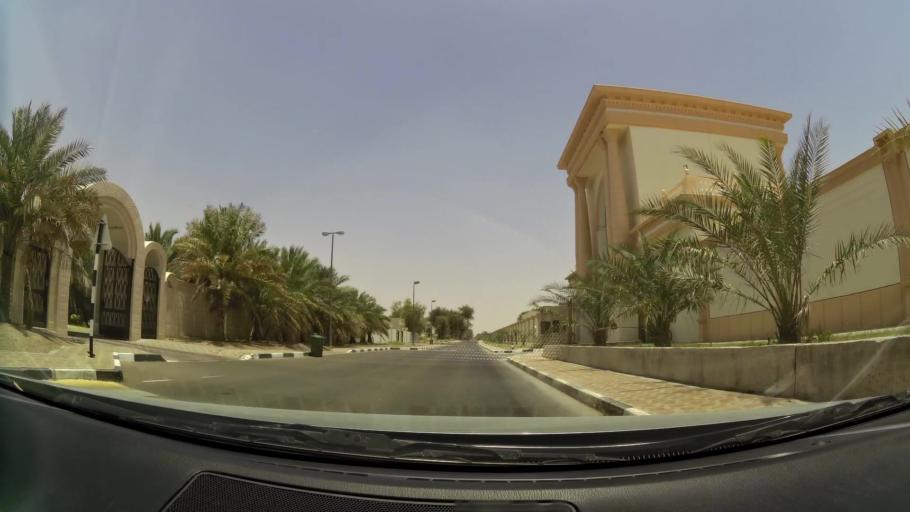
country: OM
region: Al Buraimi
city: Al Buraymi
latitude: 24.2788
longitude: 55.7369
